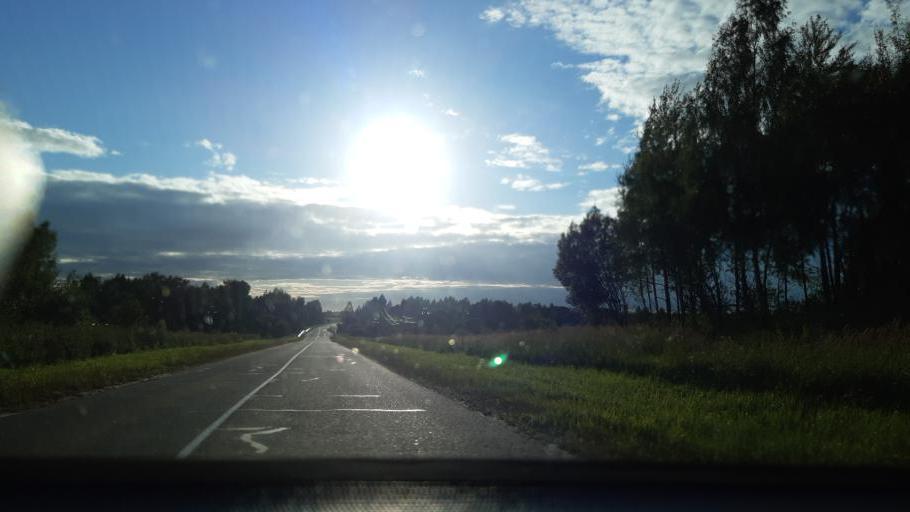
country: RU
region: Smolensk
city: Yel'nya
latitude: 54.5590
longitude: 33.1739
